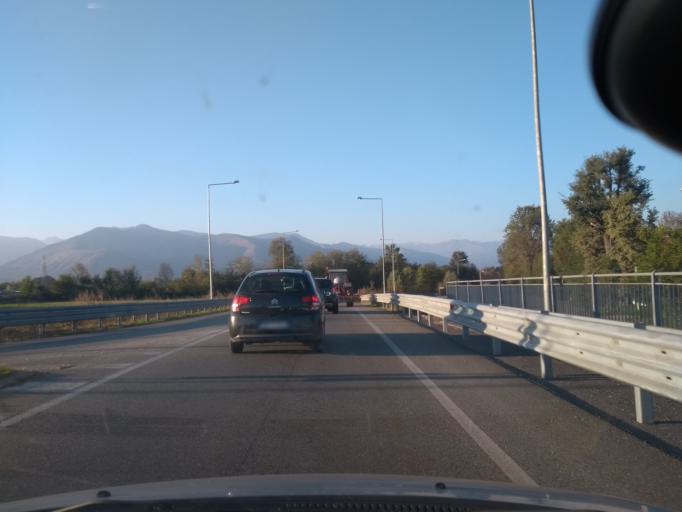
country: IT
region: Piedmont
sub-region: Provincia di Torino
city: Pianezza
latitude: 45.1185
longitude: 7.5428
